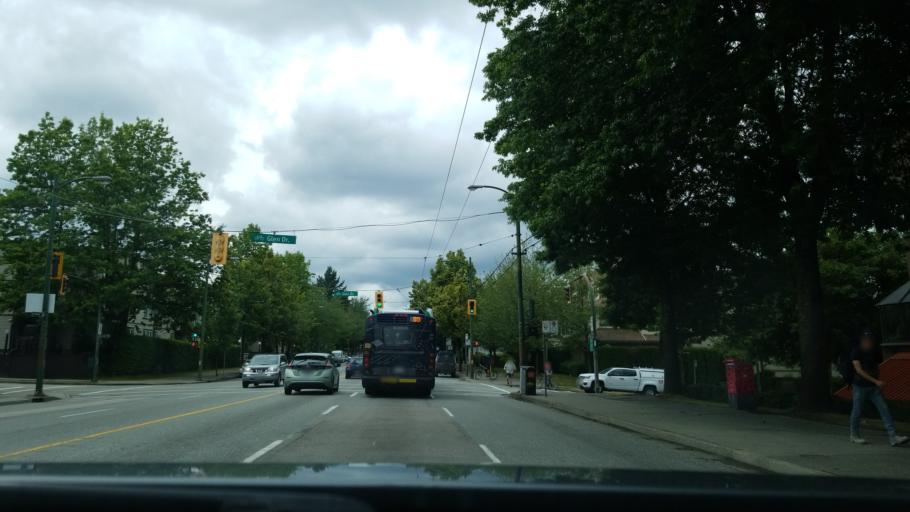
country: CA
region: British Columbia
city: Vancouver
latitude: 49.2624
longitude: -123.0808
